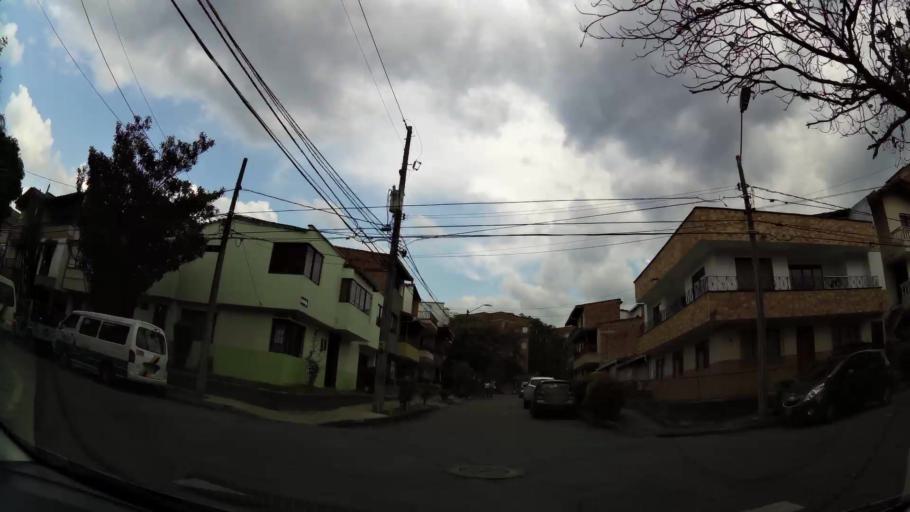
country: CO
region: Antioquia
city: Envigado
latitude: 6.1652
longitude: -75.5882
